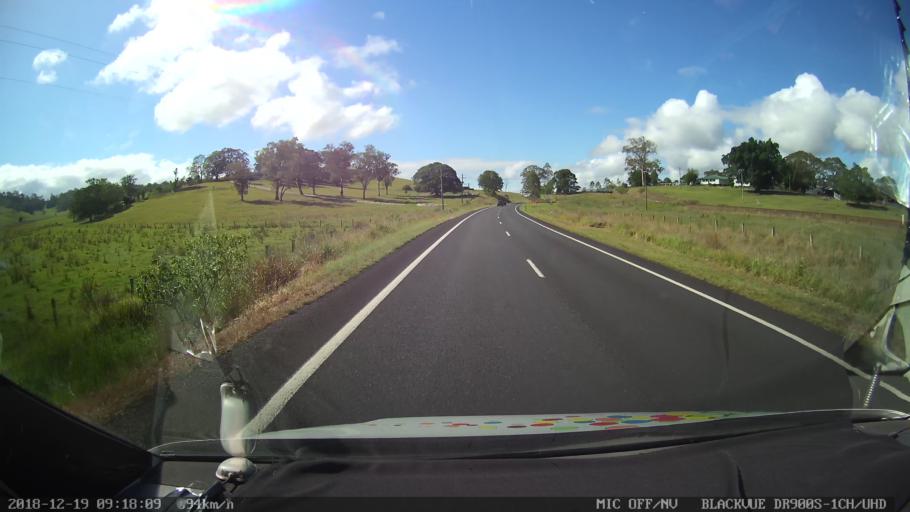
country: AU
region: New South Wales
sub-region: Kyogle
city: Kyogle
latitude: -28.5431
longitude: 152.9768
